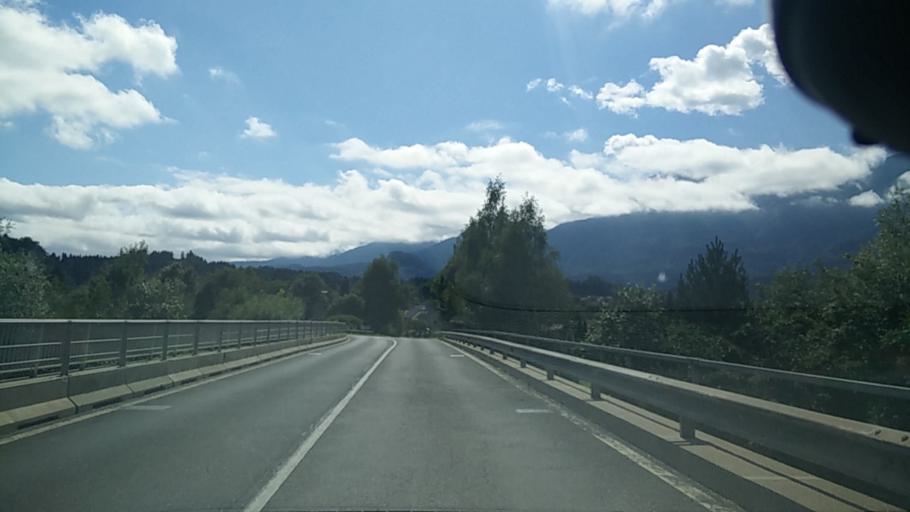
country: AT
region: Carinthia
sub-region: Politischer Bezirk Villach Land
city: Finkenstein am Faaker See
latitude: 46.5711
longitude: 13.8422
